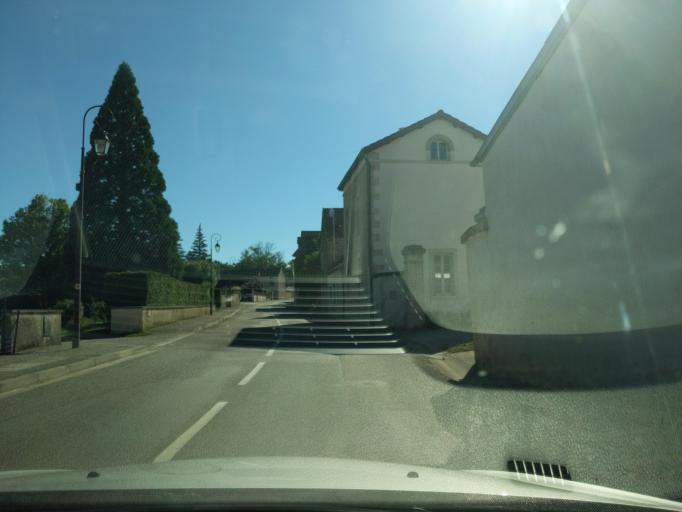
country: FR
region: Bourgogne
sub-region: Departement de la Cote-d'Or
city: Is-sur-Tille
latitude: 47.5222
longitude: 5.0643
